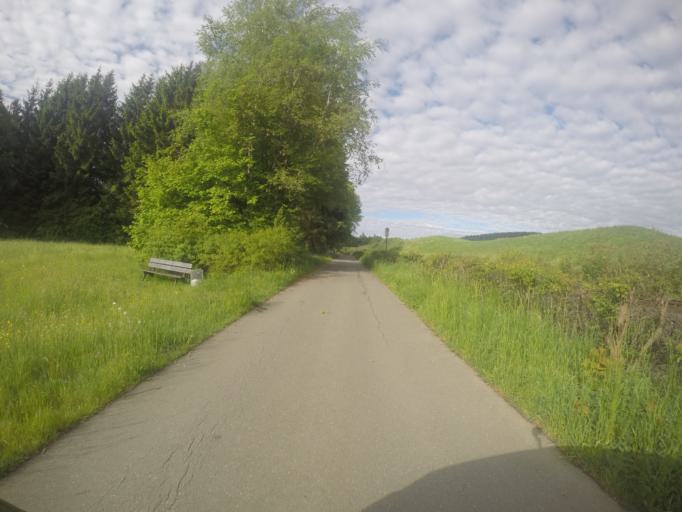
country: DE
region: Bavaria
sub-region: Upper Franconia
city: Schonwald
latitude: 50.2083
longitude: 12.1003
